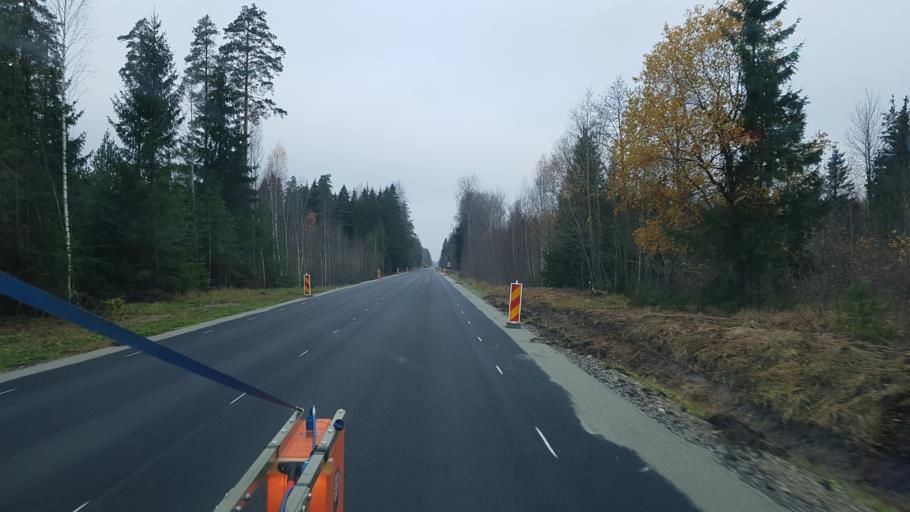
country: EE
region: Paernumaa
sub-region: Vaendra vald (alev)
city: Vandra
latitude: 58.8285
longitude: 25.1116
